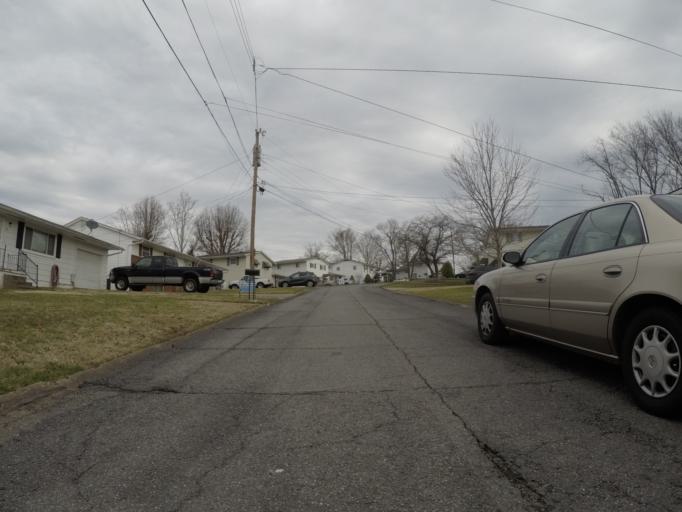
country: US
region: West Virginia
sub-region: Cabell County
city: Pea Ridge
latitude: 38.3918
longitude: -82.3791
